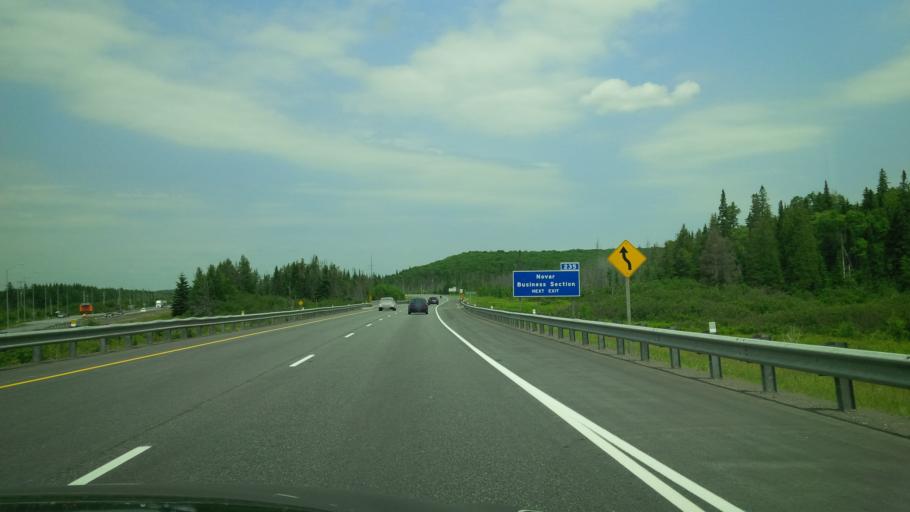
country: CA
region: Ontario
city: Huntsville
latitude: 45.4269
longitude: -79.2383
